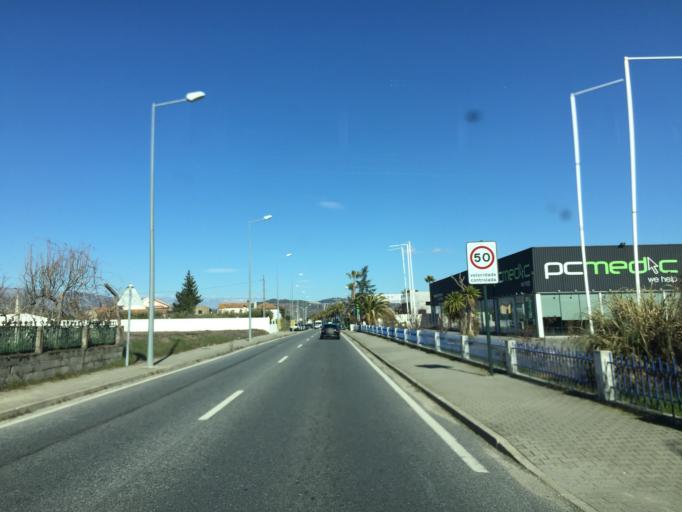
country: PT
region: Castelo Branco
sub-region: Concelho do Fundao
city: Fundao
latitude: 40.1648
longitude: -7.4968
